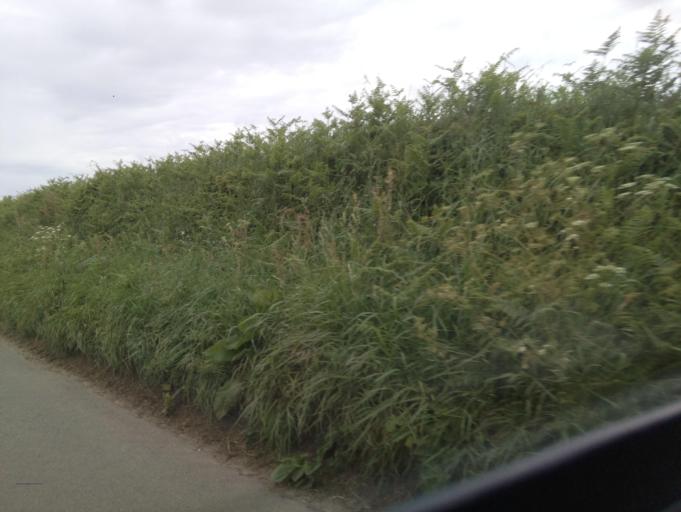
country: GB
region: England
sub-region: Devon
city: Dartmouth
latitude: 50.3411
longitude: -3.6543
